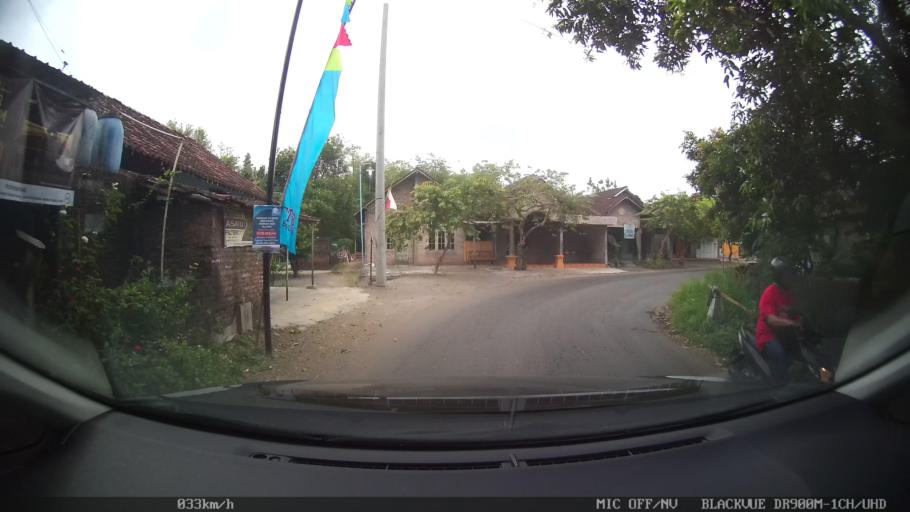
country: ID
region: Daerah Istimewa Yogyakarta
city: Sewon
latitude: -7.8705
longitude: 110.4171
